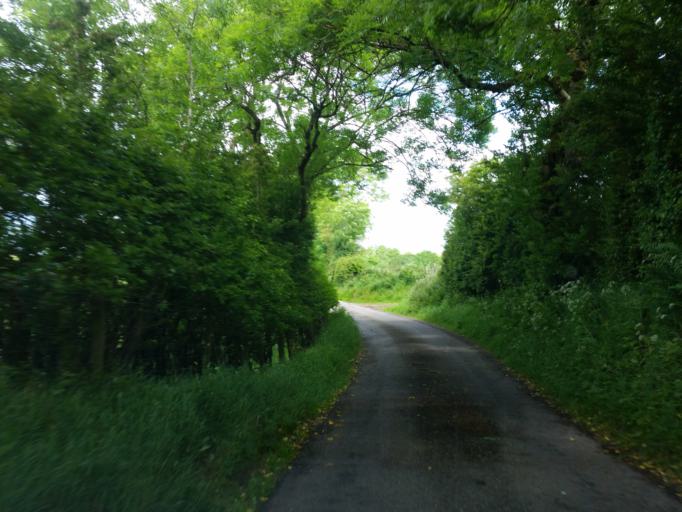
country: GB
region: Northern Ireland
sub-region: Omagh District
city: Omagh
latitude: 54.5564
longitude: -7.0851
